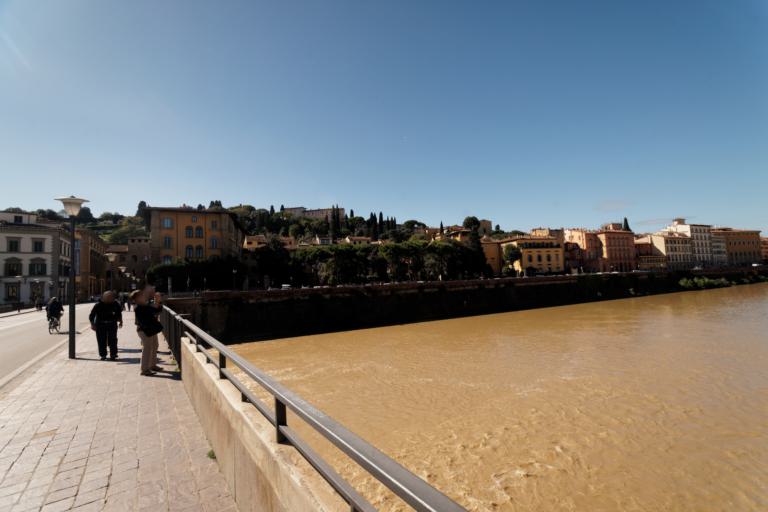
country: IT
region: Tuscany
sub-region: Province of Florence
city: Florence
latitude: 43.7662
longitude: 11.2587
